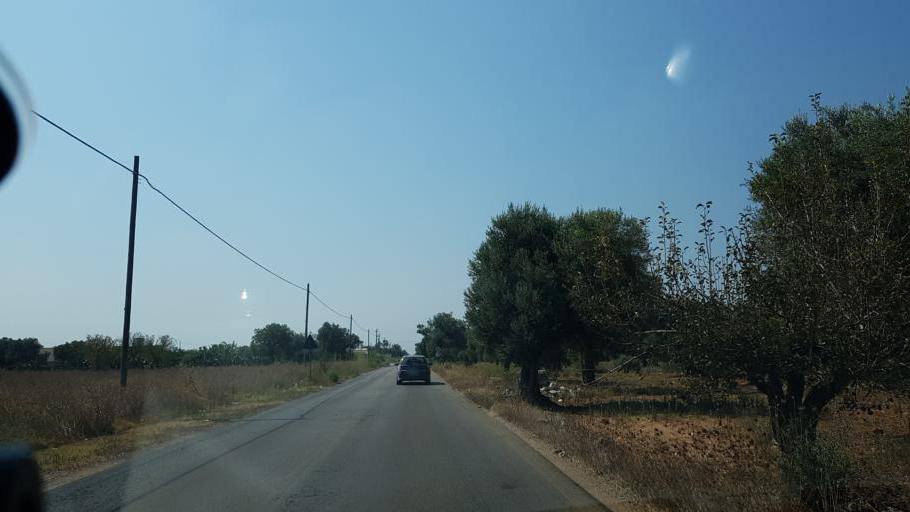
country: IT
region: Apulia
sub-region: Provincia di Taranto
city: Manduria
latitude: 40.4175
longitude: 17.6322
